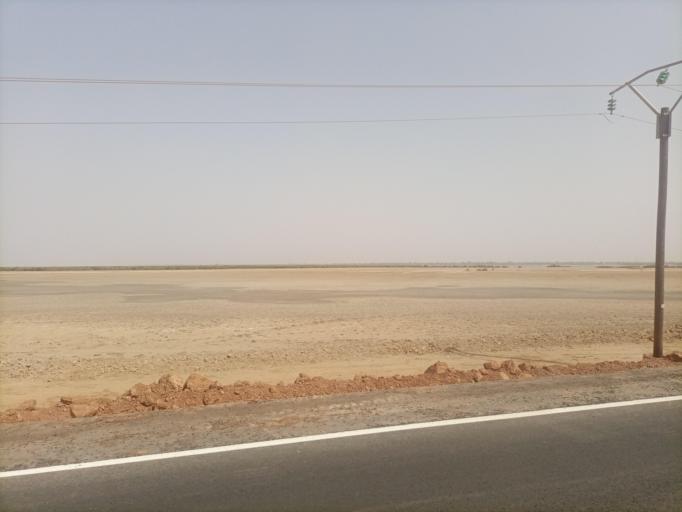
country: SN
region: Fatick
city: Foundiougne
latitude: 14.1466
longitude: -16.4717
